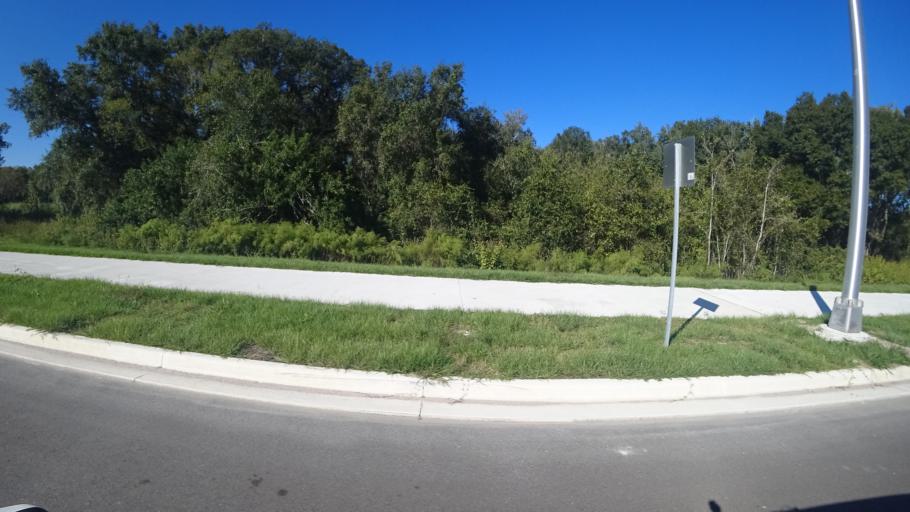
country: US
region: Florida
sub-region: Manatee County
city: Ellenton
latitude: 27.5824
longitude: -82.4357
